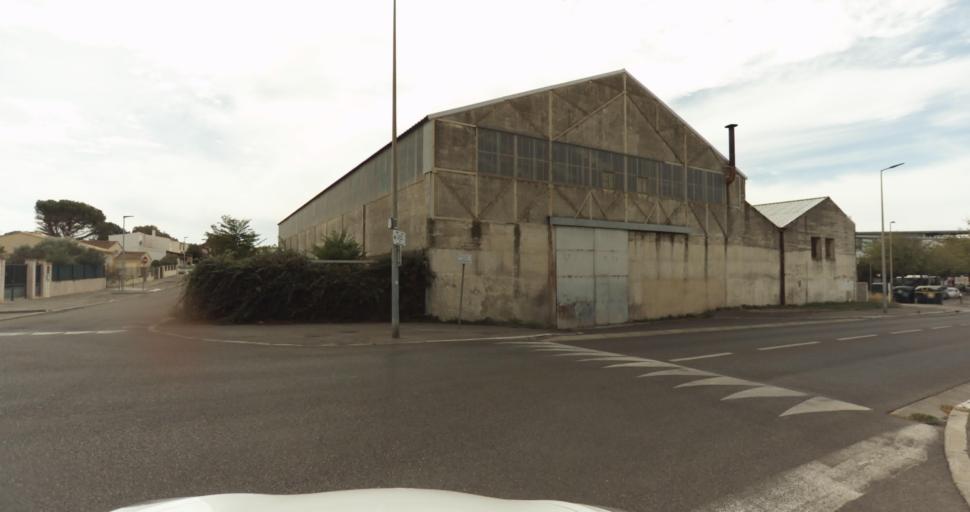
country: FR
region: Provence-Alpes-Cote d'Azur
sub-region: Departement des Bouches-du-Rhone
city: Miramas
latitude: 43.5743
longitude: 5.0021
